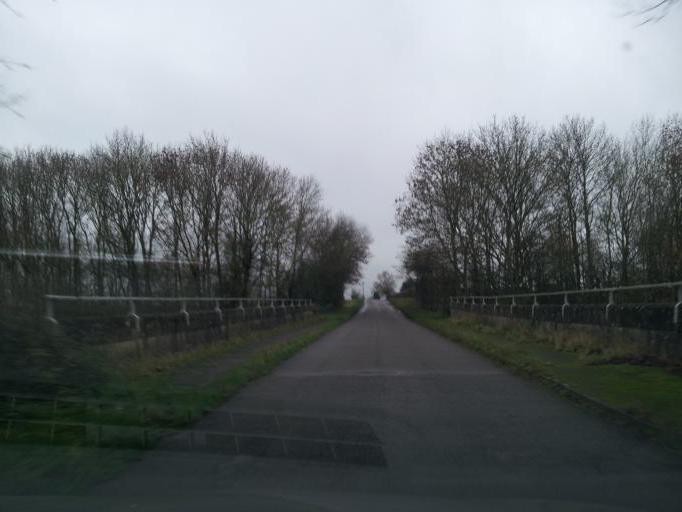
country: GB
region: England
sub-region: Warwickshire
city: Rugby
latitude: 52.3360
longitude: -1.1981
